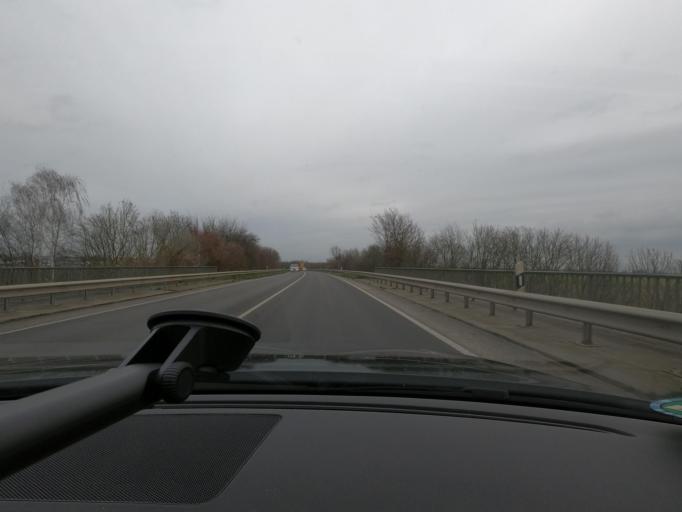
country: DE
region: North Rhine-Westphalia
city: Kempen
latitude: 51.3601
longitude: 6.4426
